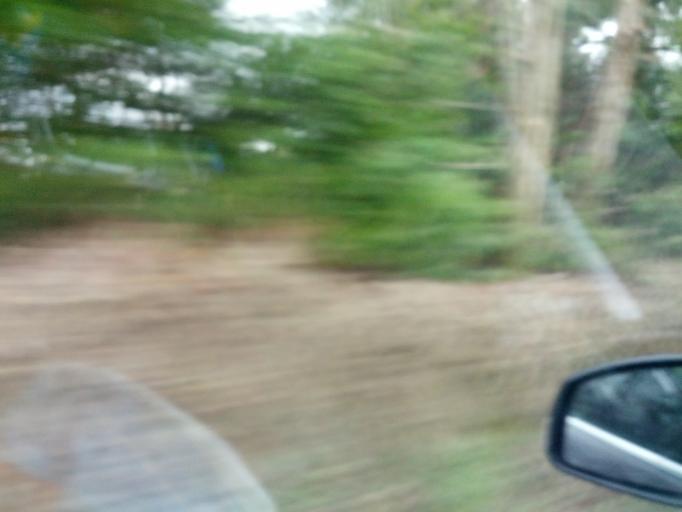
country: IE
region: Connaught
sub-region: County Galway
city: Oranmore
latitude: 53.2299
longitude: -8.8428
